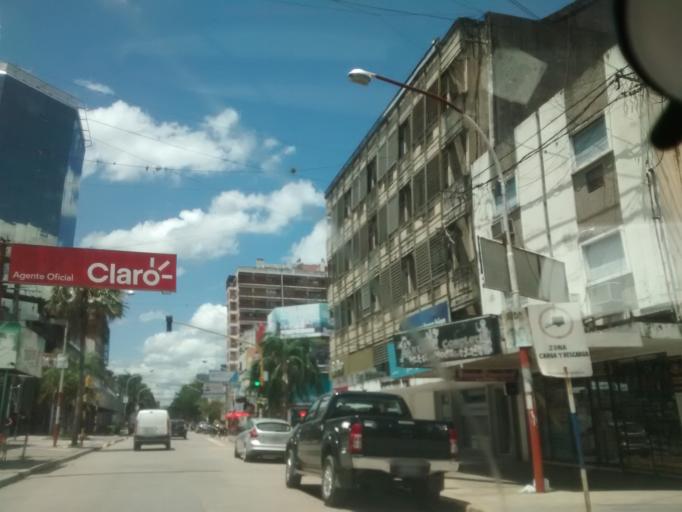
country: AR
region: Chaco
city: Resistencia
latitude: -27.4538
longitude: -58.9877
